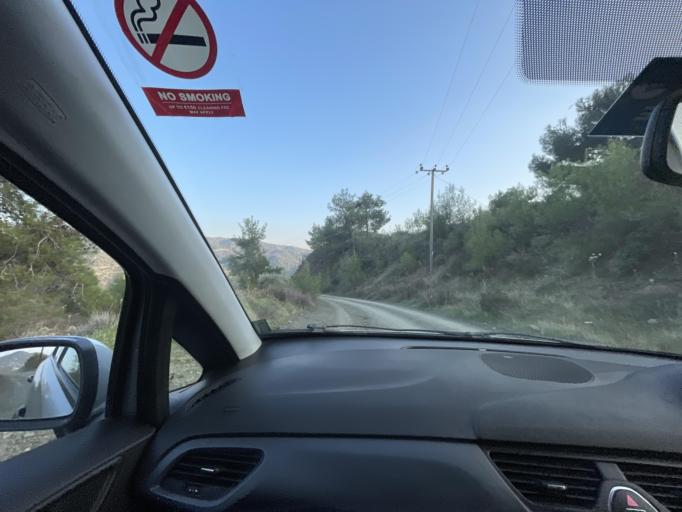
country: CY
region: Limassol
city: Pelendri
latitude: 34.8857
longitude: 32.9739
